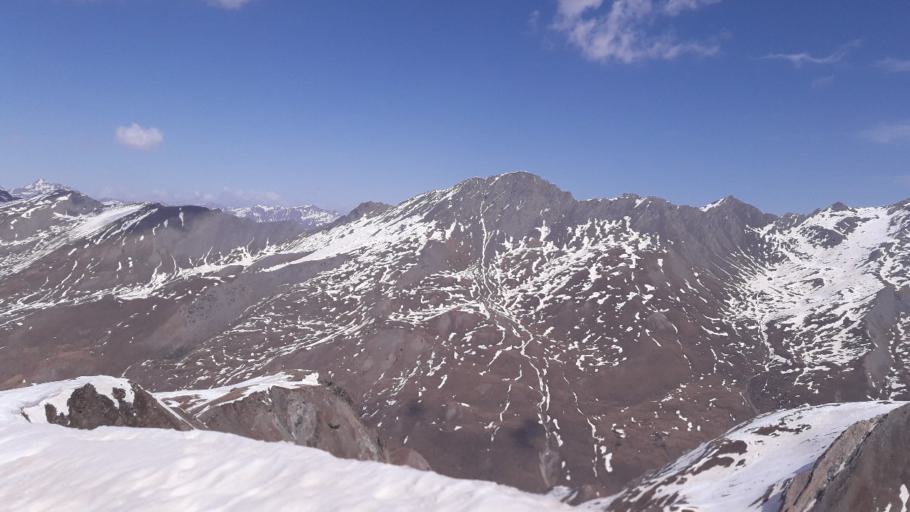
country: IT
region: Piedmont
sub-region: Provincia di Cuneo
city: Pontechianale
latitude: 44.6903
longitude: 6.9266
